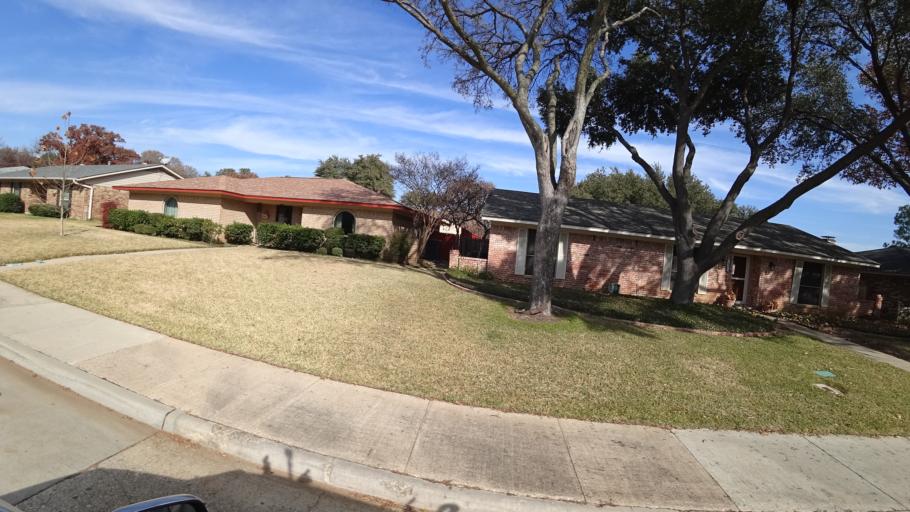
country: US
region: Texas
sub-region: Denton County
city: Lewisville
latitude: 33.0461
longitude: -97.0286
